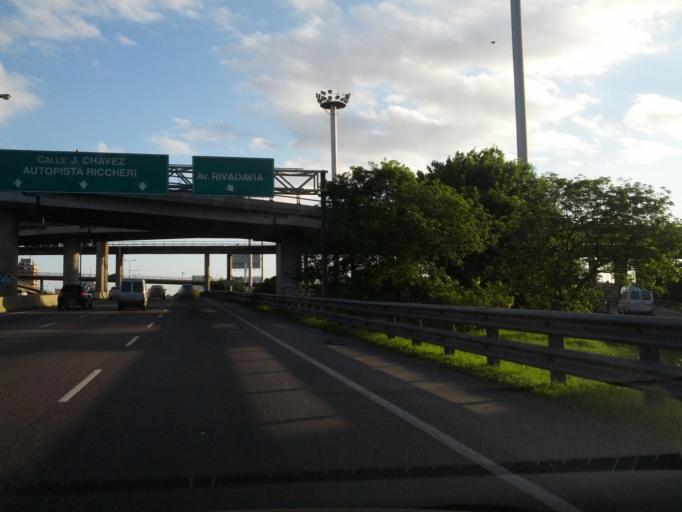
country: AR
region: Buenos Aires
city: Caseros
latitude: -34.6336
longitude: -58.5301
